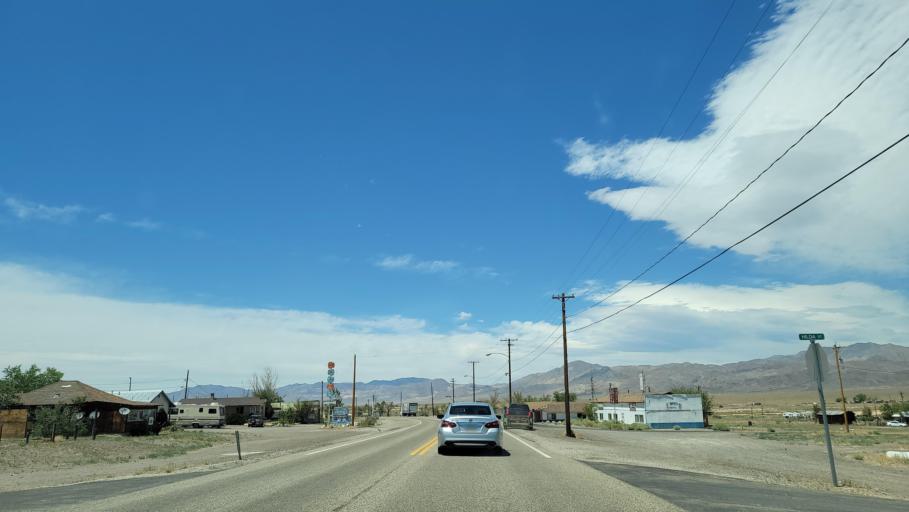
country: US
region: Nevada
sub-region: Mineral County
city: Hawthorne
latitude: 38.3864
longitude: -118.1070
